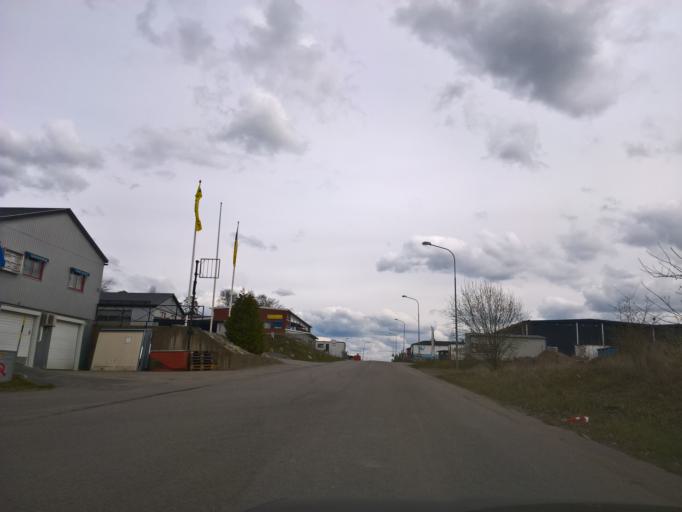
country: SE
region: OEstergoetland
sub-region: Finspangs Kommun
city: Finspang
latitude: 58.7008
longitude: 15.8043
